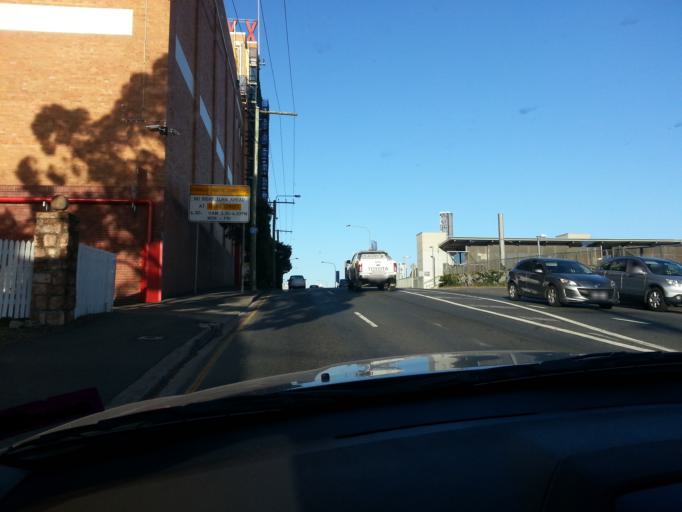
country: AU
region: Queensland
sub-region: Brisbane
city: Milton
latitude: -27.4688
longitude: 153.0045
